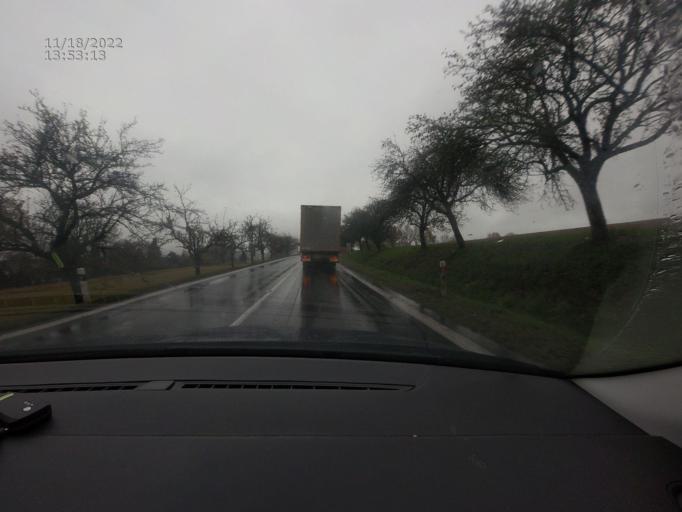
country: CZ
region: Jihocesky
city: Sedlice
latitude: 49.3934
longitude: 13.9179
